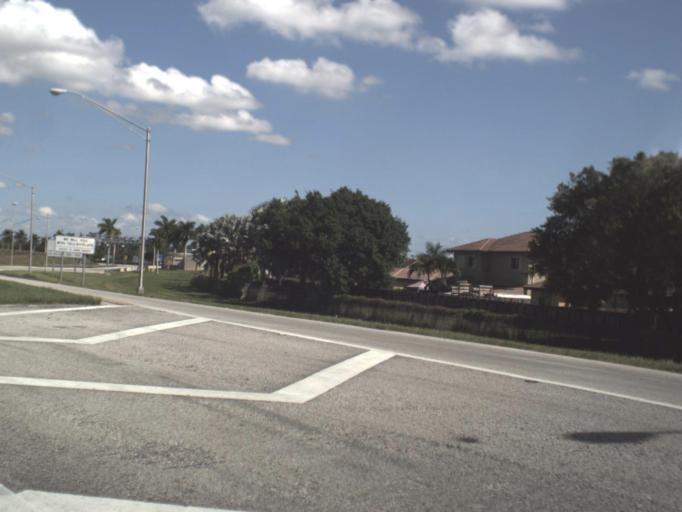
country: US
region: Florida
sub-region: Miami-Dade County
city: Leisure City
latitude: 25.4957
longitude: -80.4177
